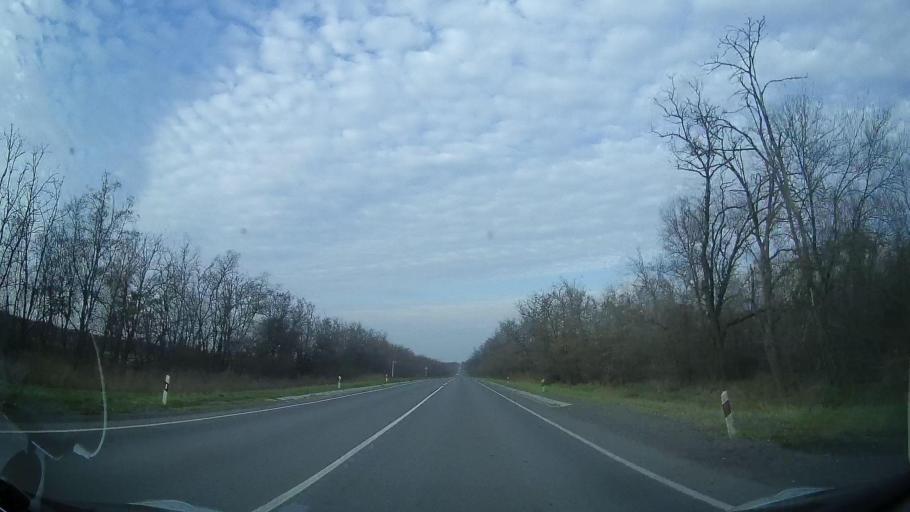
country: RU
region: Rostov
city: Bagayevskaya
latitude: 47.1040
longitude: 40.2767
